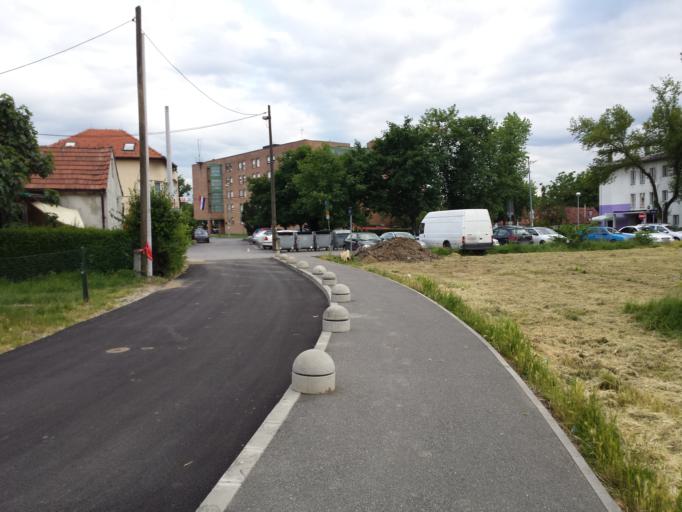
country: HR
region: Grad Zagreb
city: Novi Zagreb
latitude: 45.7981
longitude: 15.9891
